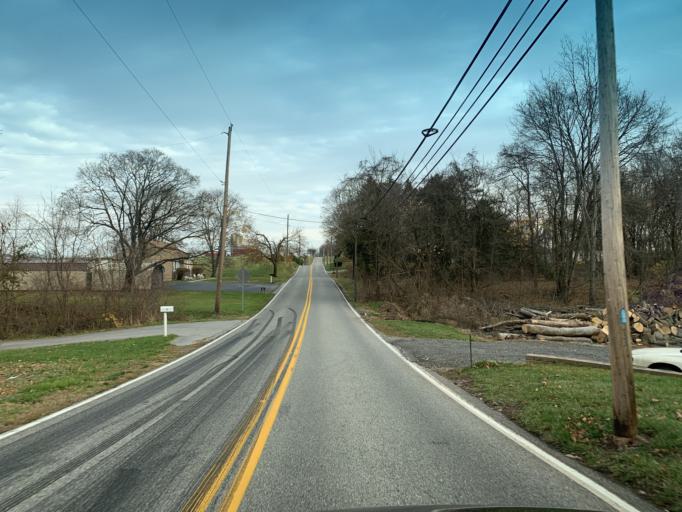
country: US
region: Pennsylvania
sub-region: York County
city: Manchester
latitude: 40.0879
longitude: -76.7616
